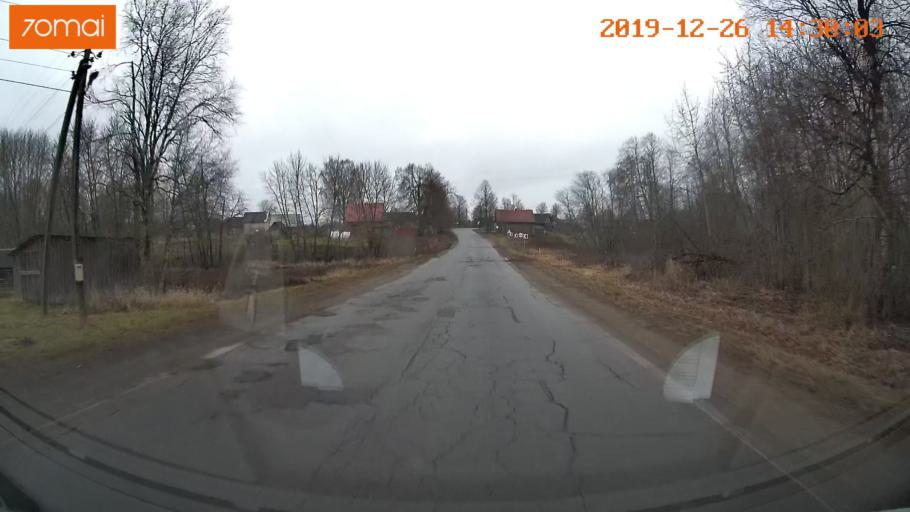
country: RU
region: Jaroslavl
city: Poshekhon'ye
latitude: 58.4571
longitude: 39.0388
